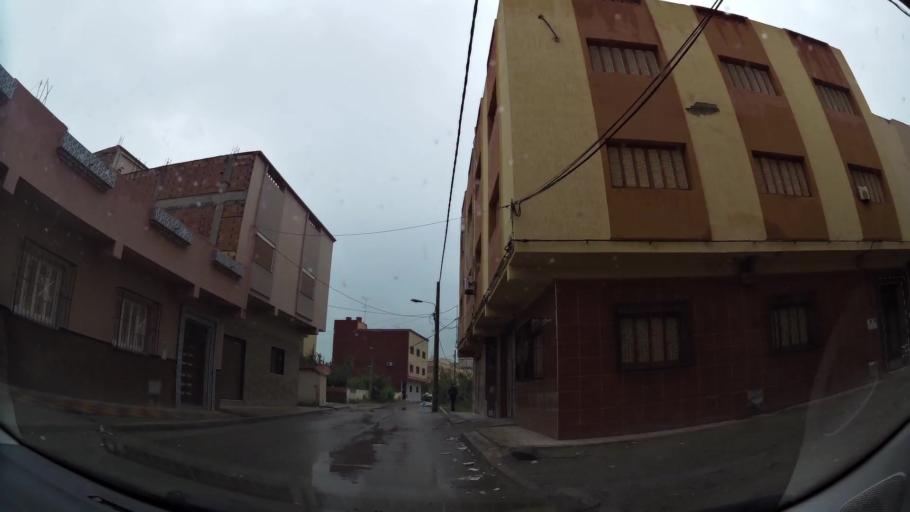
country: MA
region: Oriental
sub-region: Nador
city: Nador
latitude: 35.1614
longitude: -2.9531
